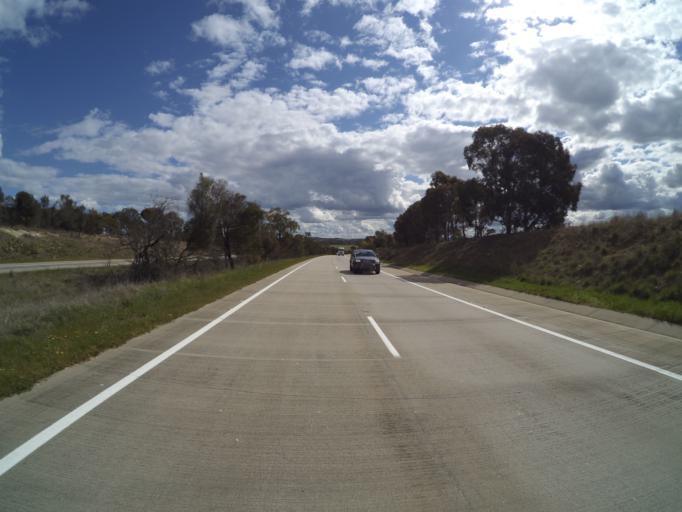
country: AU
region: New South Wales
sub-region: Yass Valley
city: Murrumbateman
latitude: -34.7882
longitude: 149.1995
